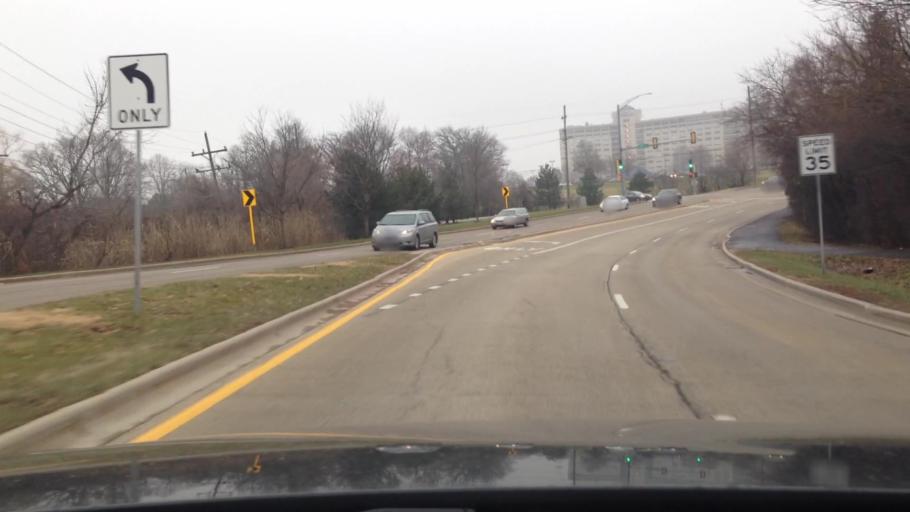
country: US
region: Illinois
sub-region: DuPage County
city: Oakbrook Terrace
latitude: 41.8258
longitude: -87.9716
